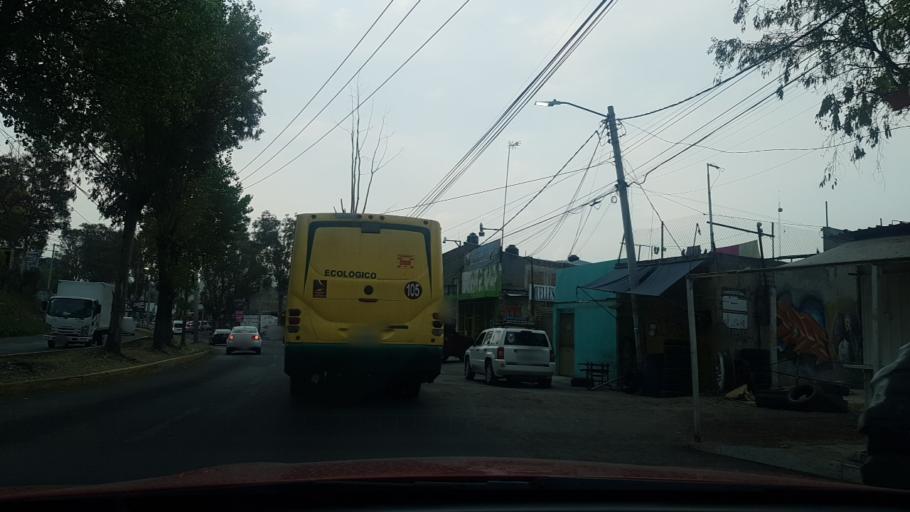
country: MX
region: Mexico
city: Cuautitlan Izcalli
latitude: 19.6055
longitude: -99.2249
